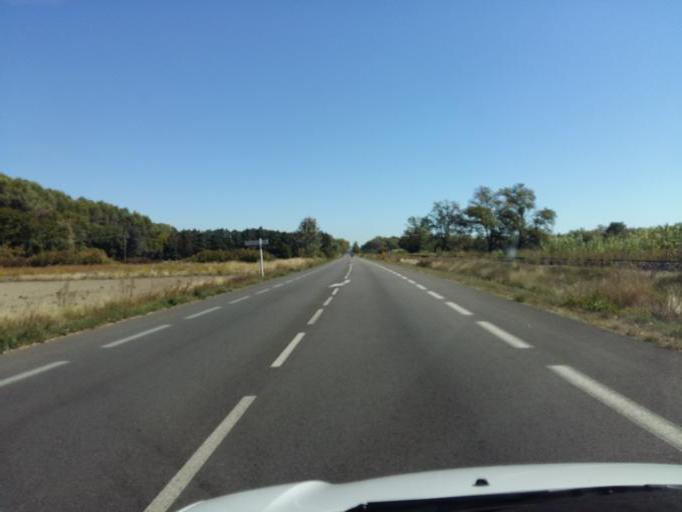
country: FR
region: Provence-Alpes-Cote d'Azur
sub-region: Departement du Vaucluse
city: Merindol
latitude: 43.7547
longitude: 5.2370
